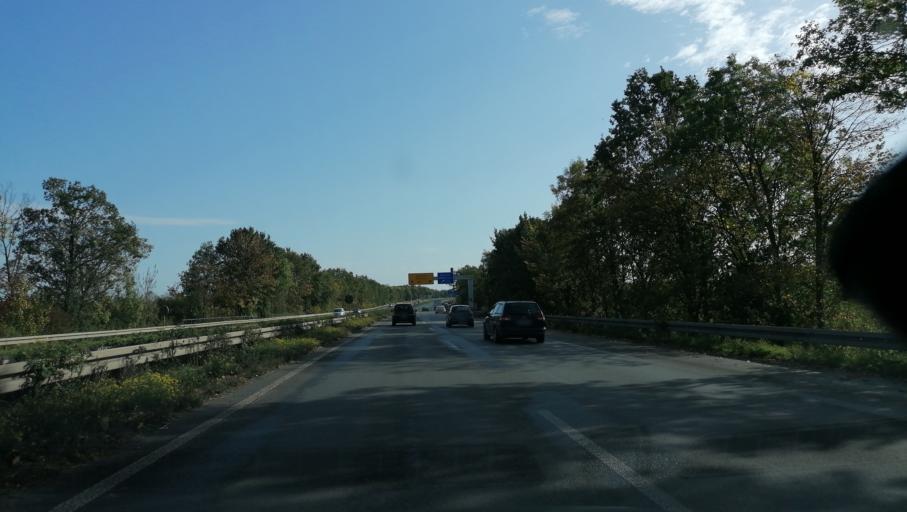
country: DE
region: North Rhine-Westphalia
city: Lunen
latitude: 51.5846
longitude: 7.4879
